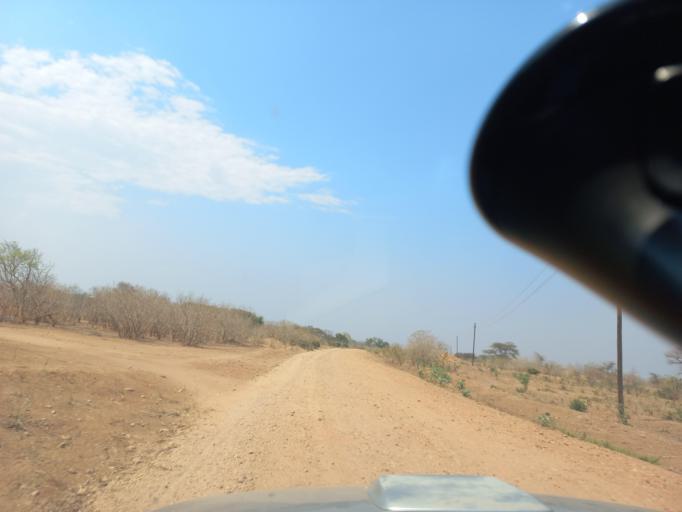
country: ZW
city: Chirundu
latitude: -15.9390
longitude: 28.8538
